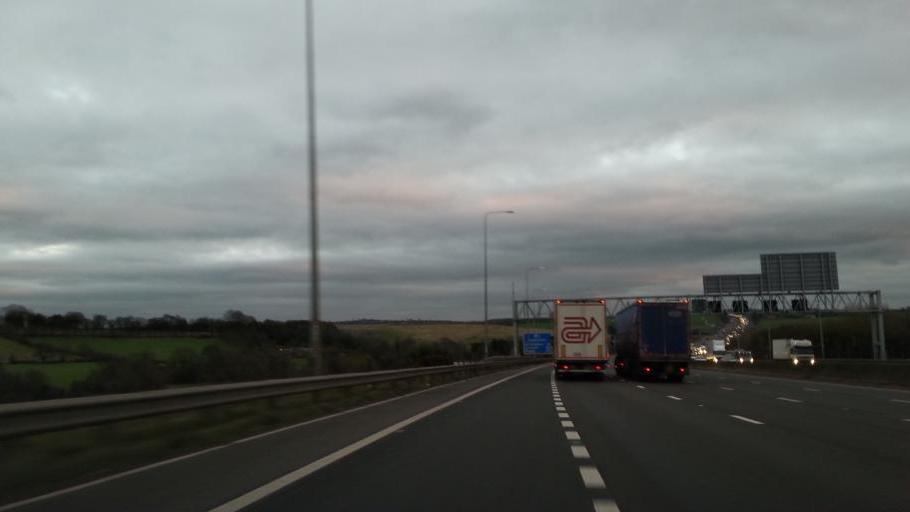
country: GB
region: England
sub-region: Derbyshire
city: Pinxton
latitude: 53.0963
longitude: -1.3125
